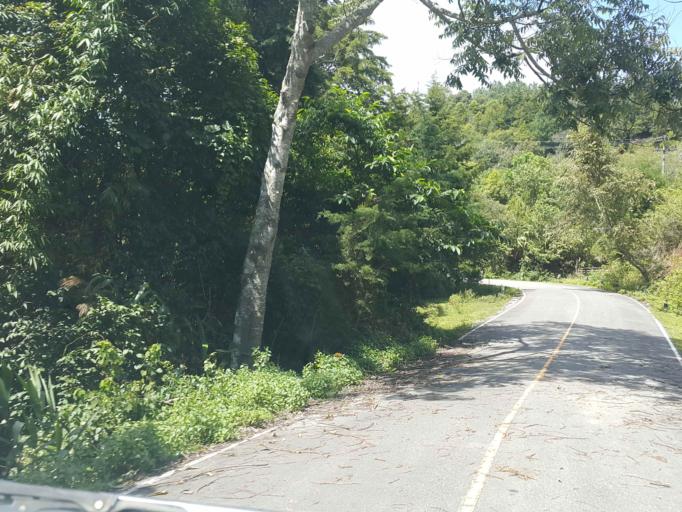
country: TH
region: Chiang Mai
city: Mae Chaem
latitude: 18.5155
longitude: 98.5294
